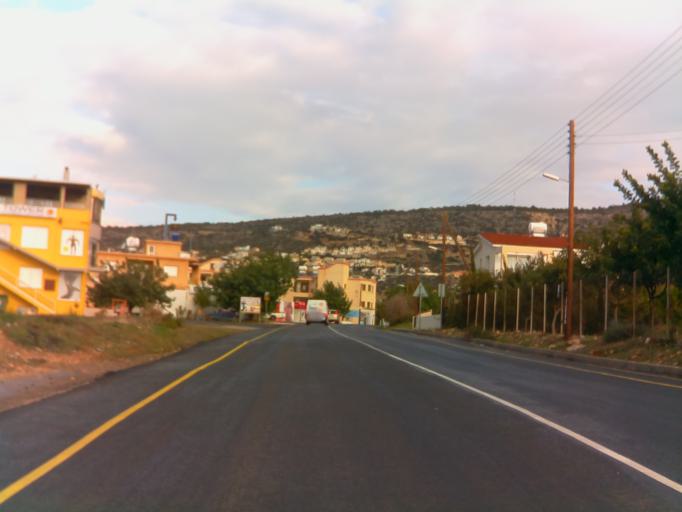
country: CY
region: Pafos
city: Pegeia
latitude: 34.8704
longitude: 32.3783
